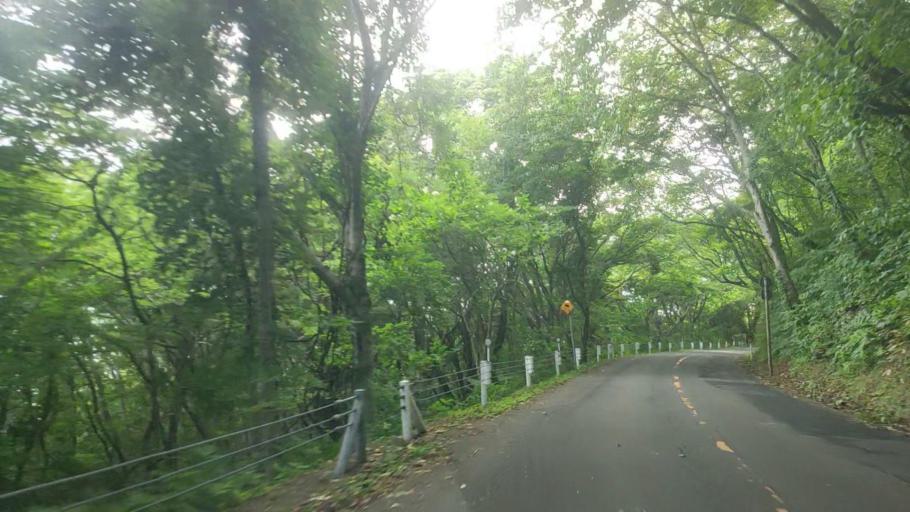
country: JP
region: Hokkaido
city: Hakodate
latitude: 41.7626
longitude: 140.7036
